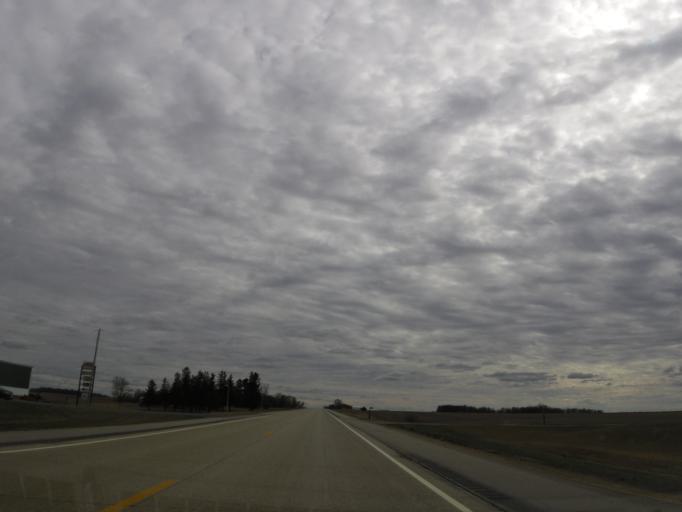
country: US
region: Minnesota
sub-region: Fillmore County
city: Spring Valley
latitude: 43.5232
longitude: -92.3694
